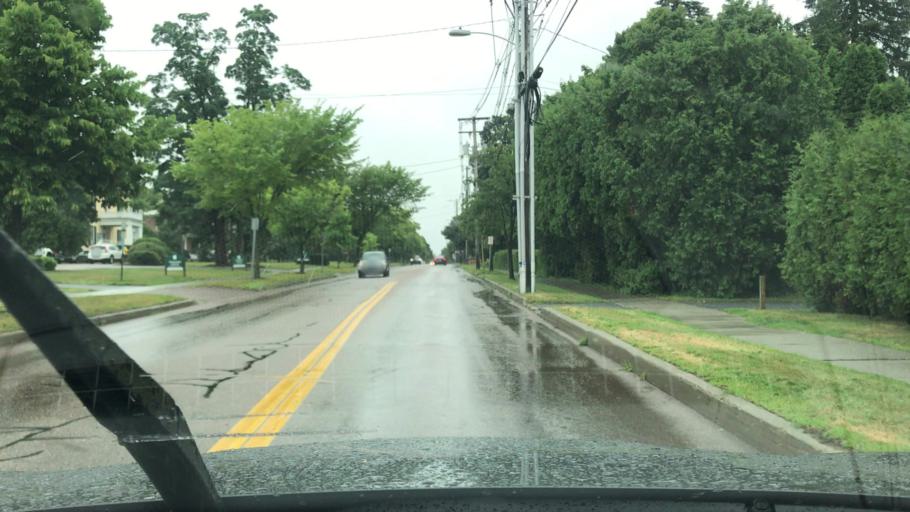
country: US
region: Vermont
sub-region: Chittenden County
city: Burlington
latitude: 44.4758
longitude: -73.2007
